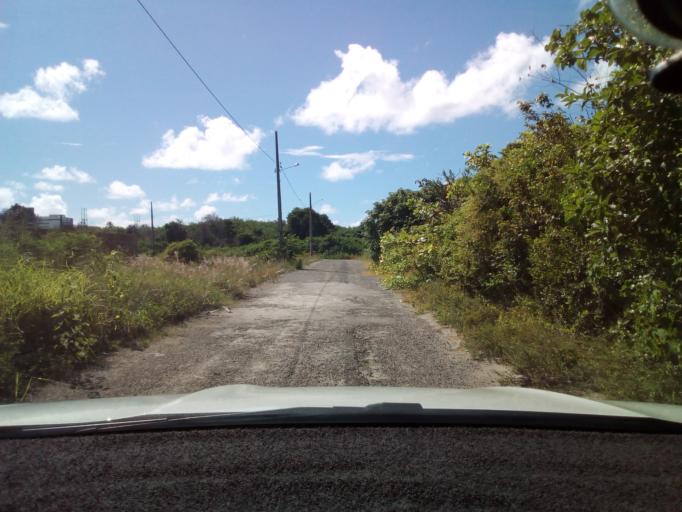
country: BR
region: Paraiba
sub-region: Joao Pessoa
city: Joao Pessoa
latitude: -7.0563
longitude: -34.8488
